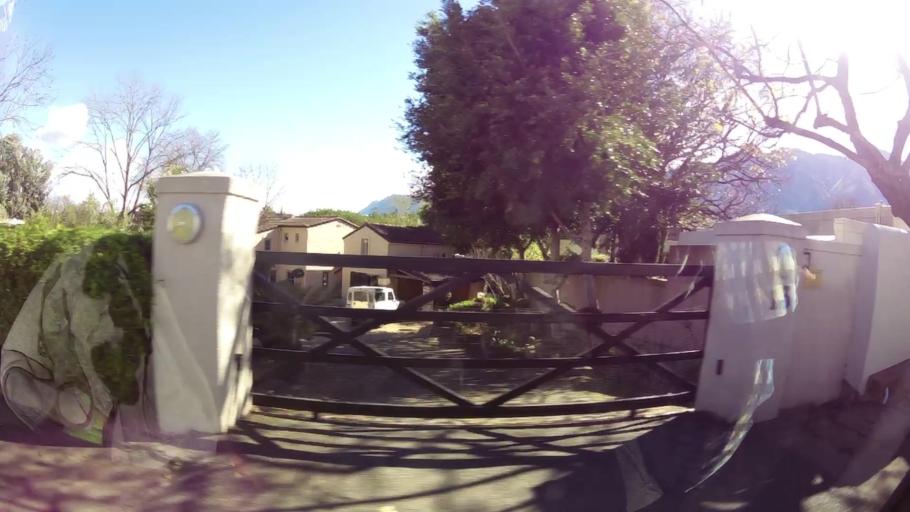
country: ZA
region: Western Cape
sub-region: Overberg District Municipality
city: Swellendam
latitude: -34.0207
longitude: 20.4512
